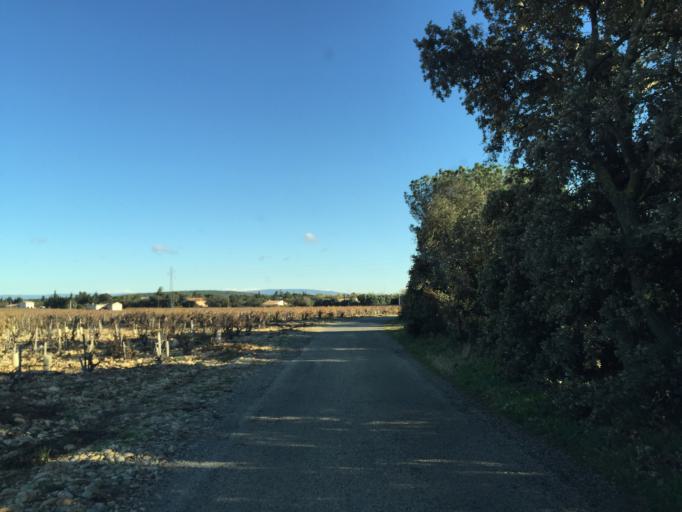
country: FR
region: Provence-Alpes-Cote d'Azur
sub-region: Departement du Vaucluse
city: Sorgues
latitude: 44.0286
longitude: 4.8501
